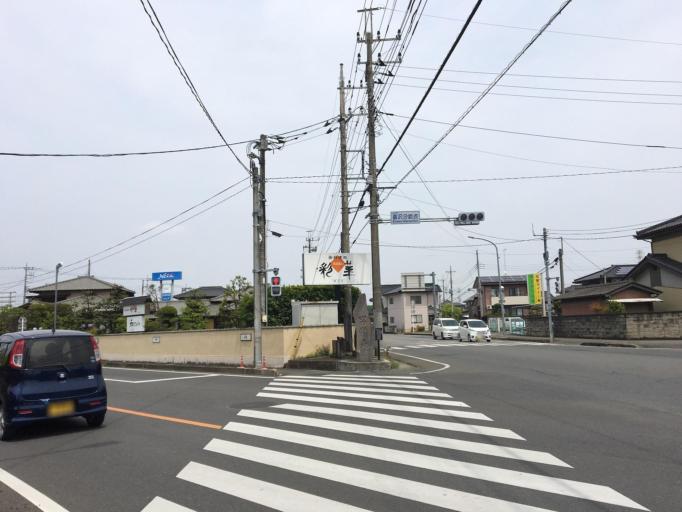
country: JP
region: Tochigi
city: Oyama
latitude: 36.3371
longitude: 139.8179
